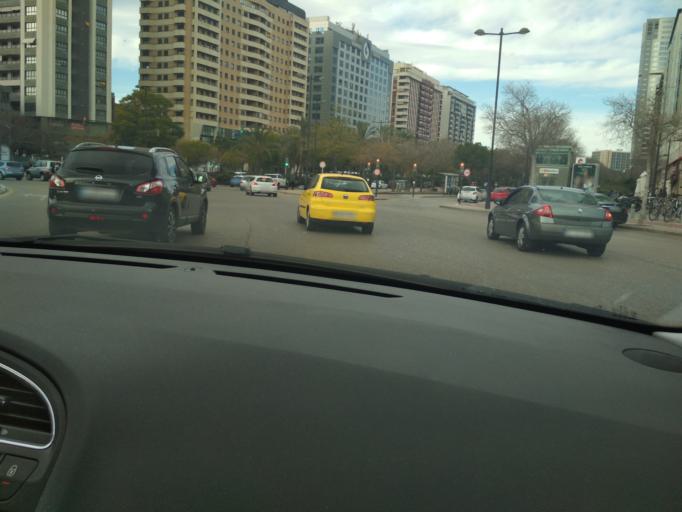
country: ES
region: Valencia
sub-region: Provincia de Valencia
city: Mislata
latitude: 39.4904
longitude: -0.3990
